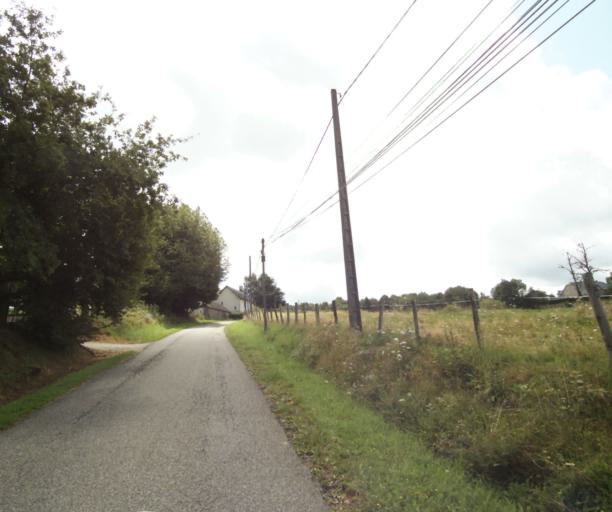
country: FR
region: Limousin
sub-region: Departement de la Correze
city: Sainte-Fortunade
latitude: 45.2024
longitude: 1.8089
